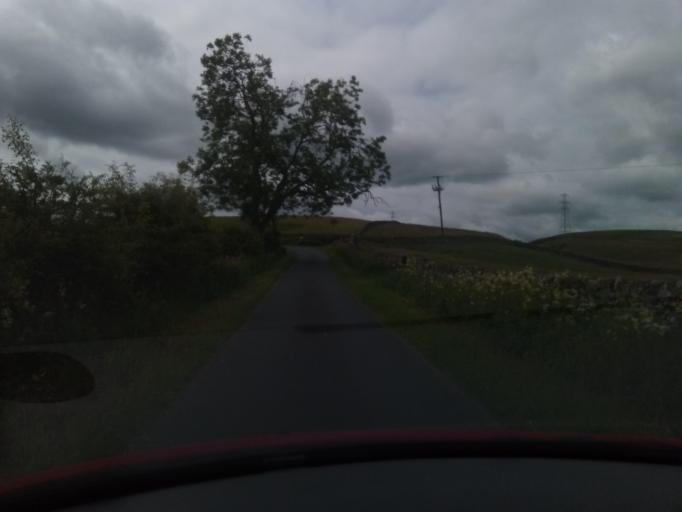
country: GB
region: Scotland
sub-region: The Scottish Borders
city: Hawick
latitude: 55.4300
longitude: -2.8202
